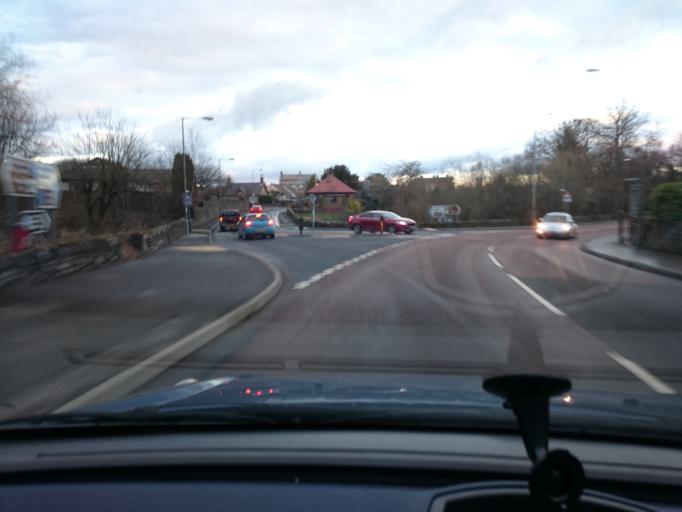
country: GB
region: Scotland
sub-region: Stirling
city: Doune
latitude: 56.1913
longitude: -4.0584
